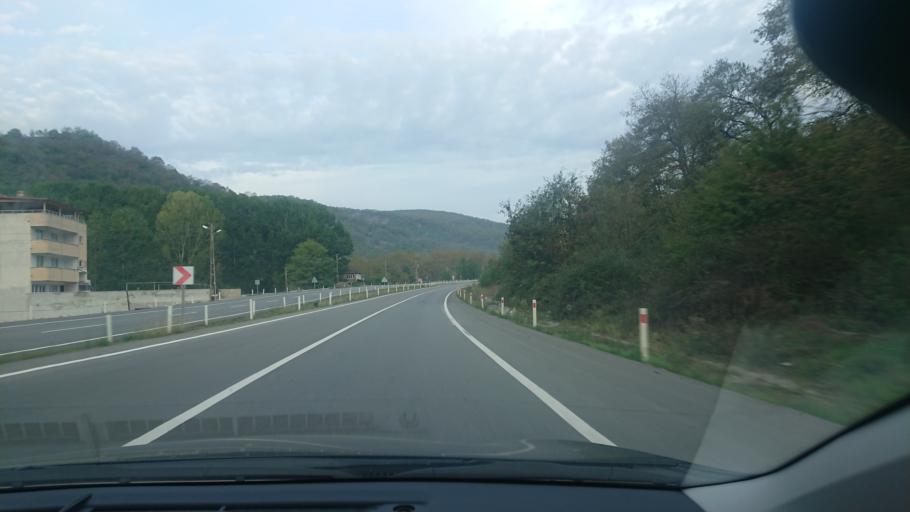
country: TR
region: Zonguldak
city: Beycuma
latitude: 41.3248
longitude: 32.0486
